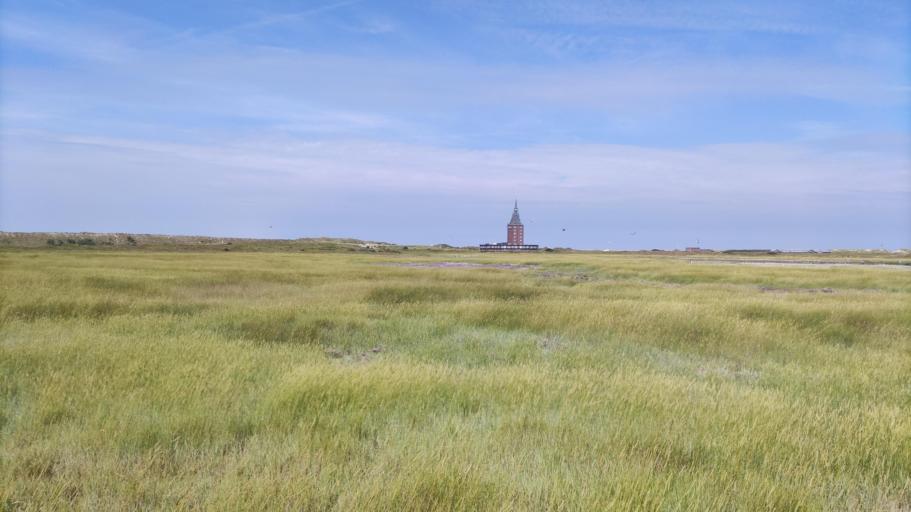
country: DE
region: Lower Saxony
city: Wangerooge
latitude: 53.7827
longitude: 7.8667
